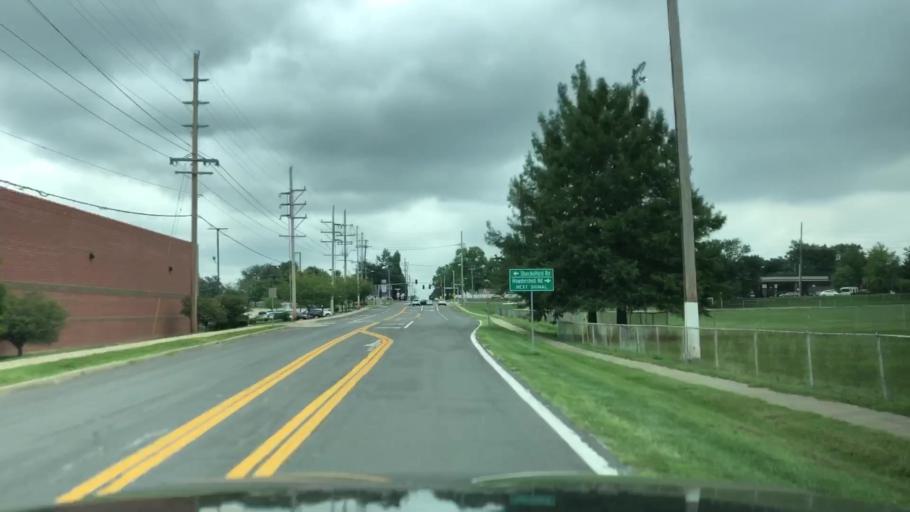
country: US
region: Missouri
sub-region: Saint Louis County
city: Hazelwood
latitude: 38.8101
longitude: -90.3608
